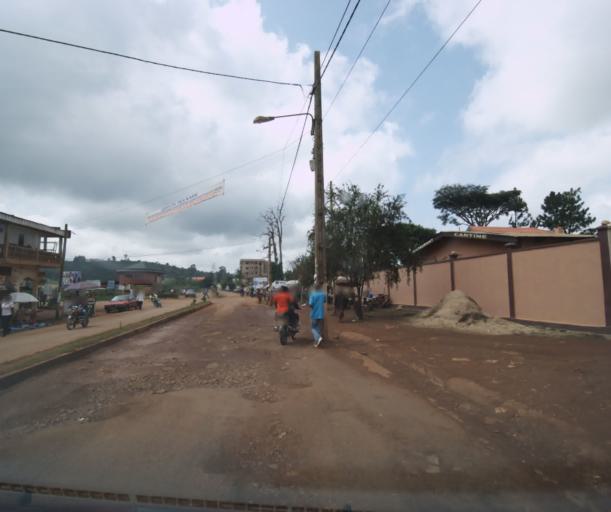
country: CM
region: West
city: Dschang
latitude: 5.4478
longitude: 10.0618
